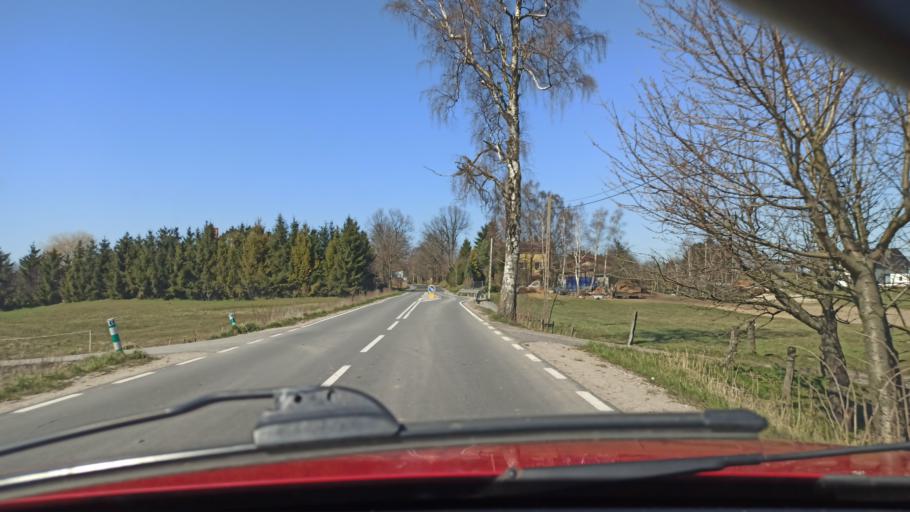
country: PL
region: Warmian-Masurian Voivodeship
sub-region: Powiat elblaski
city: Tolkmicko
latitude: 54.2127
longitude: 19.5419
